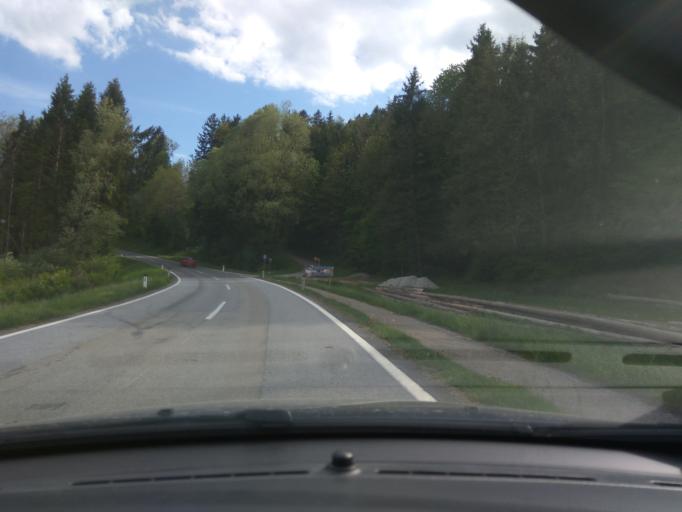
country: AT
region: Styria
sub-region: Politischer Bezirk Graz-Umgebung
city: Hitzendorf
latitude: 47.0318
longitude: 15.2956
